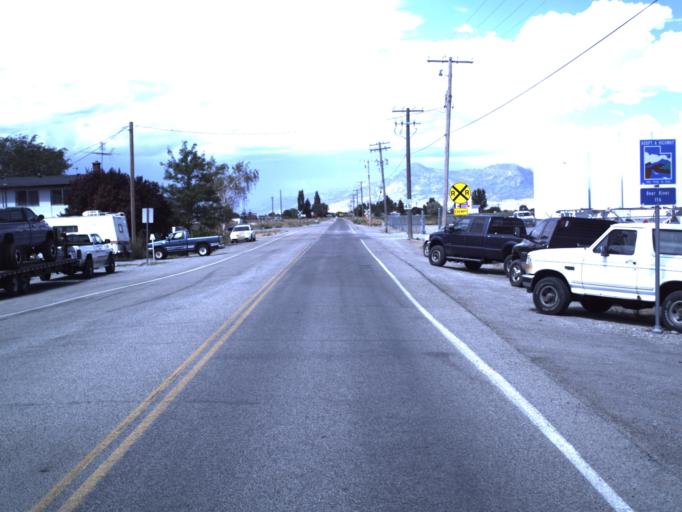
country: US
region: Utah
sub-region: Box Elder County
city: Garland
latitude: 41.7421
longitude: -112.1484
